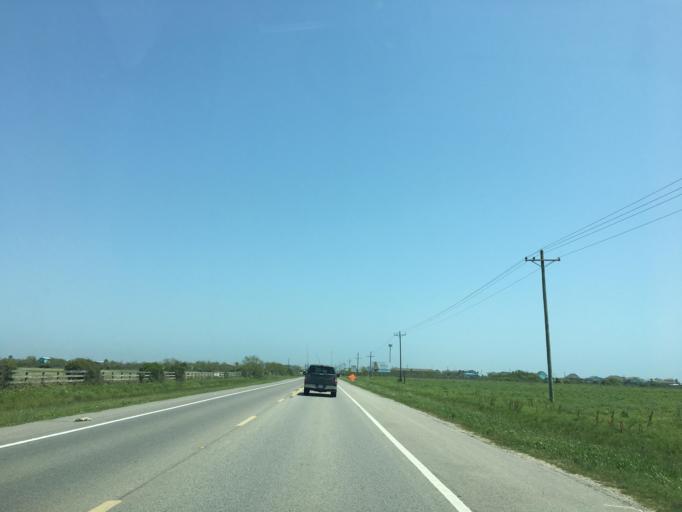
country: US
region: Texas
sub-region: Galveston County
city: Bolivar Peninsula
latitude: 29.4383
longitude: -94.6730
